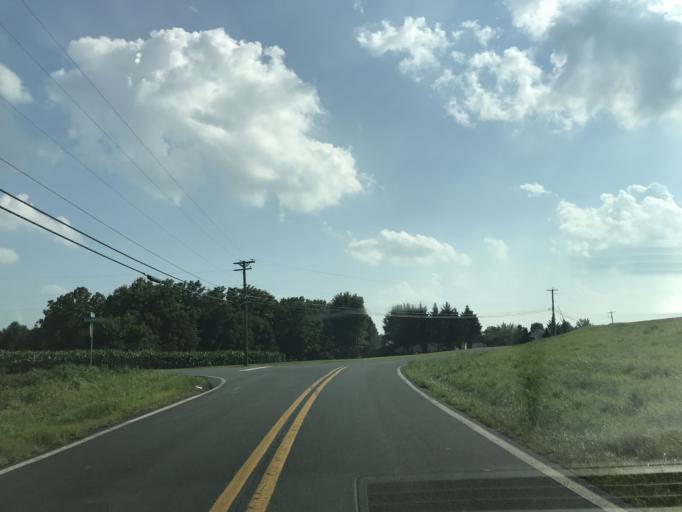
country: US
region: Maryland
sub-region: Carroll County
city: Westminster
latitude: 39.6093
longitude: -76.9854
